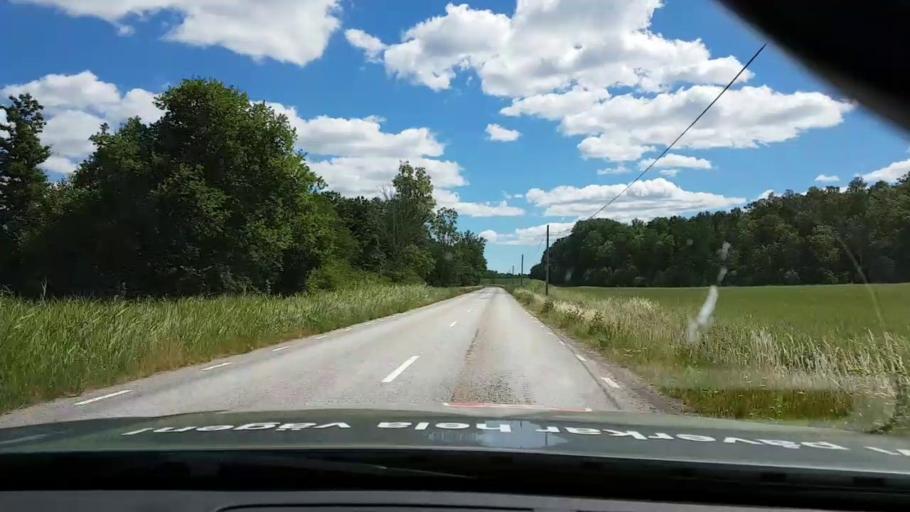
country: SE
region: Kalmar
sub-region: Vasterviks Kommun
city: Forserum
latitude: 58.0437
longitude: 16.4194
